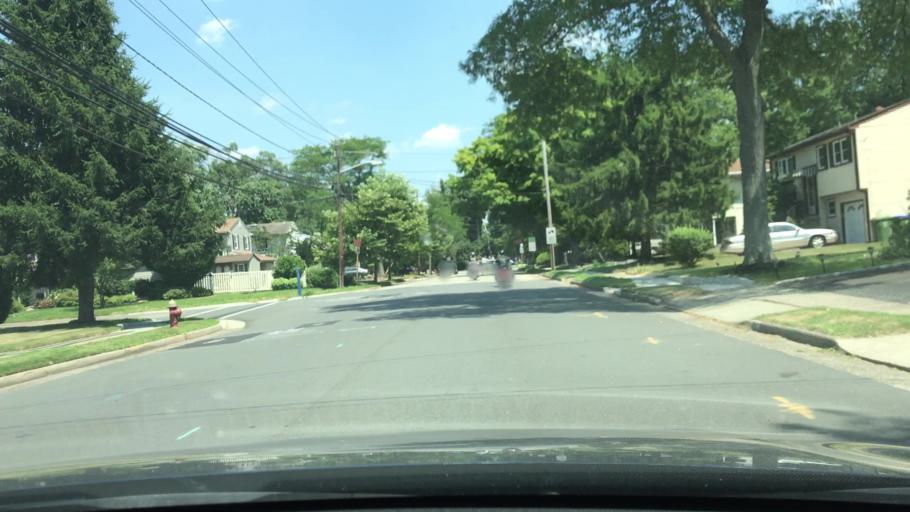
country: US
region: New Jersey
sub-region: Middlesex County
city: Metuchen
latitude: 40.5417
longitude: -74.3800
